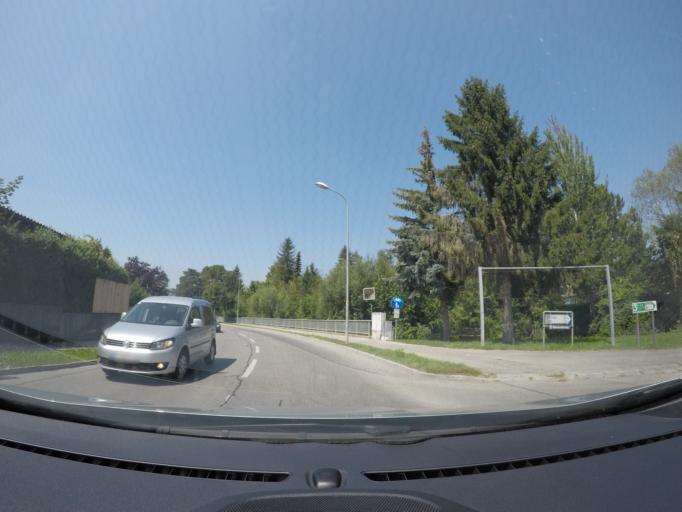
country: AT
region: Lower Austria
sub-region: Politischer Bezirk Sankt Polten
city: Eichgraben
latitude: 48.1841
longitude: 15.9649
